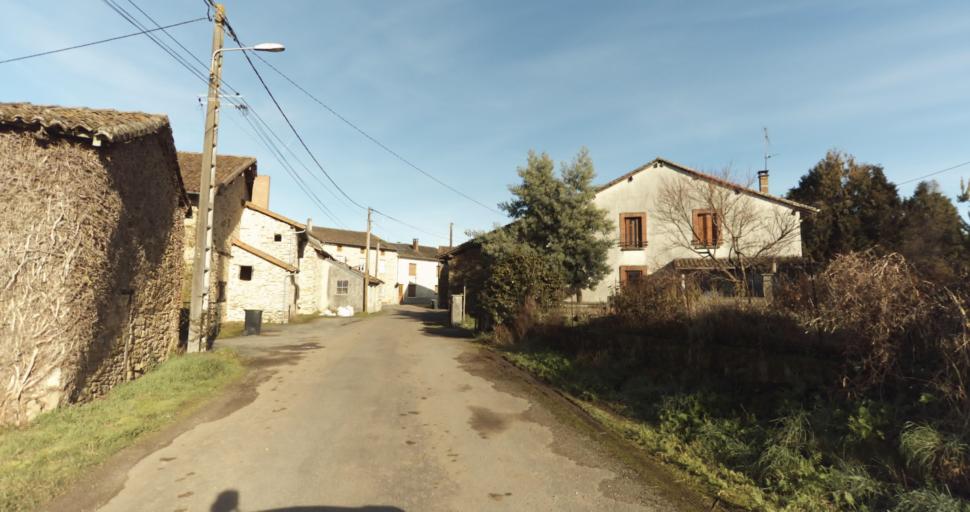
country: FR
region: Limousin
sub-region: Departement de la Haute-Vienne
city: Sereilhac
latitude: 45.7874
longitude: 1.0934
